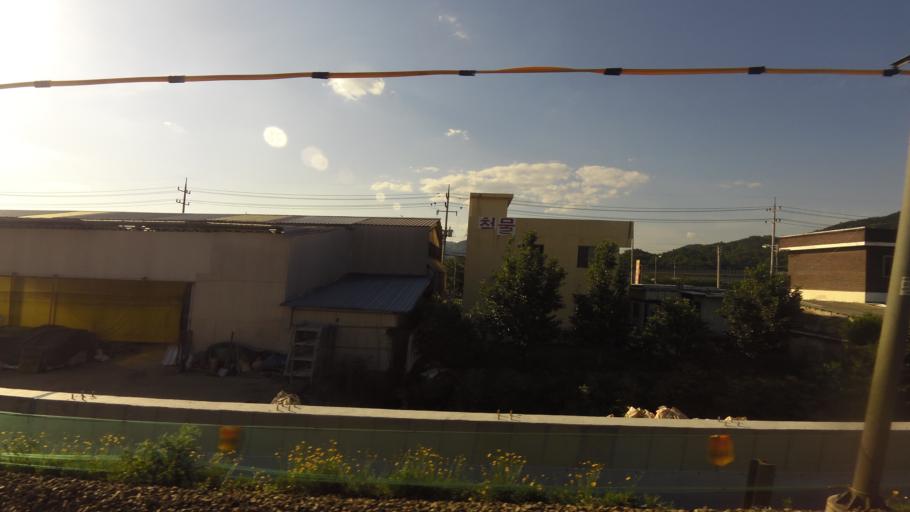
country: KR
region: Gyeongsangbuk-do
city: Gimcheon
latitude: 36.1284
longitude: 128.0990
